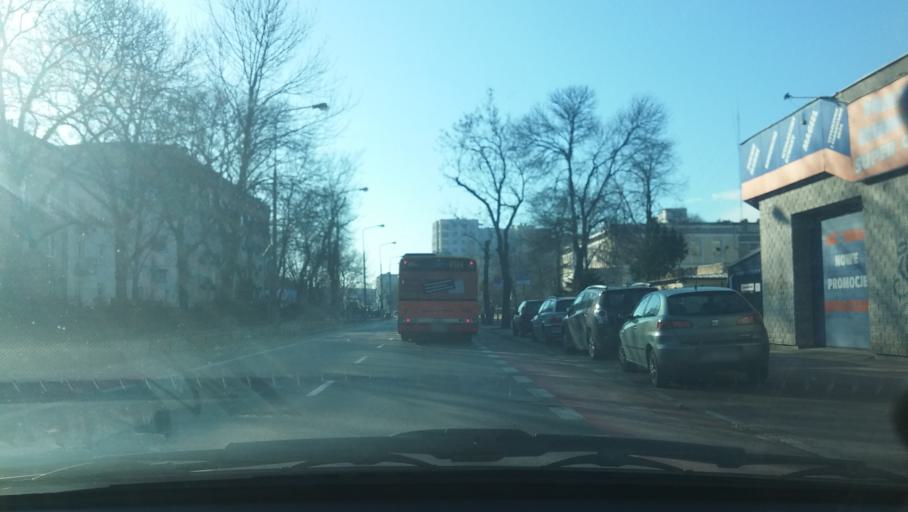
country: PL
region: Masovian Voivodeship
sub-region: Warszawa
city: Praga Poludnie
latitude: 52.2337
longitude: 21.0603
